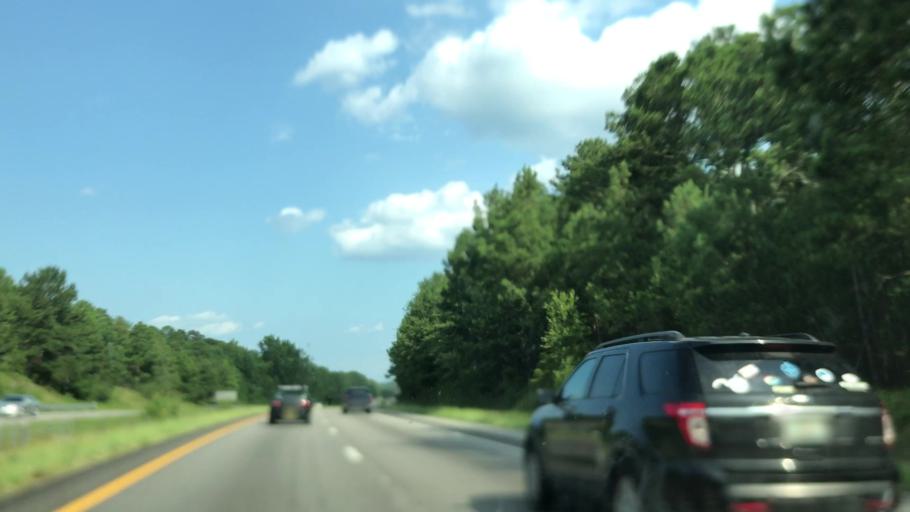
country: US
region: South Carolina
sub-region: Calhoun County
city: Oak Grove
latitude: 33.7626
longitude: -80.9581
